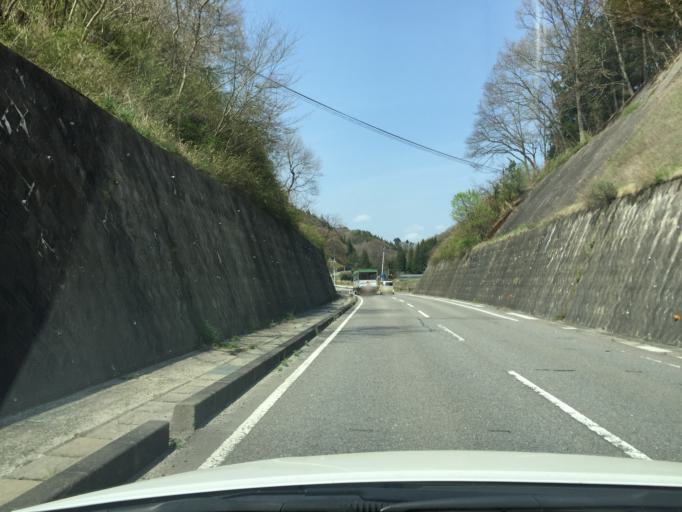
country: JP
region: Fukushima
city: Funehikimachi-funehiki
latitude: 37.4446
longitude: 140.6706
